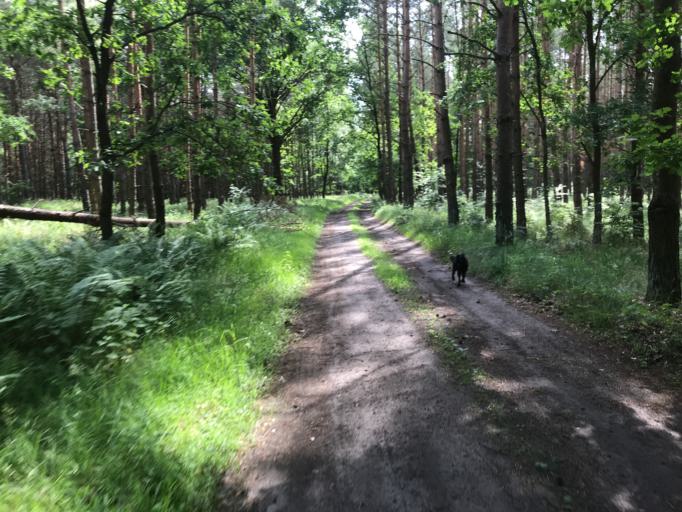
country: PL
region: West Pomeranian Voivodeship
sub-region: Powiat gryfinski
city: Mieszkowice
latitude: 52.7009
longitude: 14.4715
